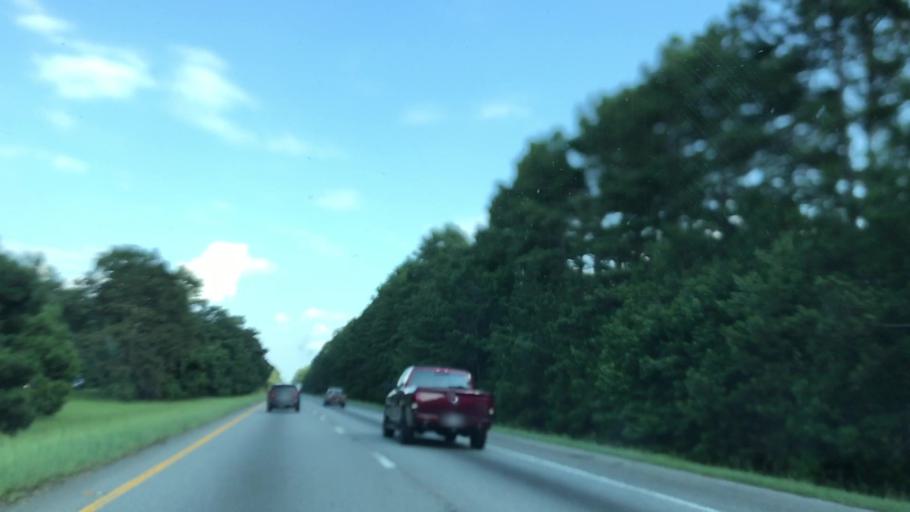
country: US
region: South Carolina
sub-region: Dorchester County
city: Saint George
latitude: 33.3756
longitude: -80.6154
